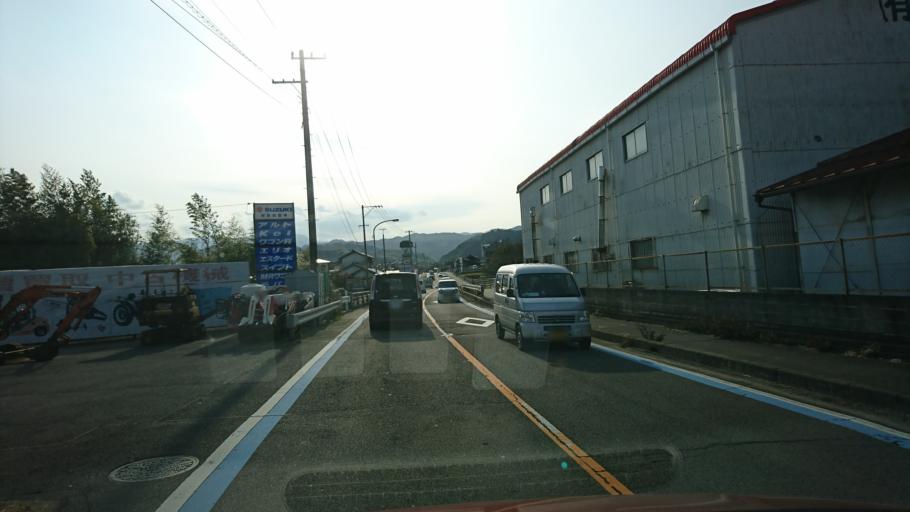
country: JP
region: Ehime
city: Hojo
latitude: 34.0239
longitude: 132.9455
